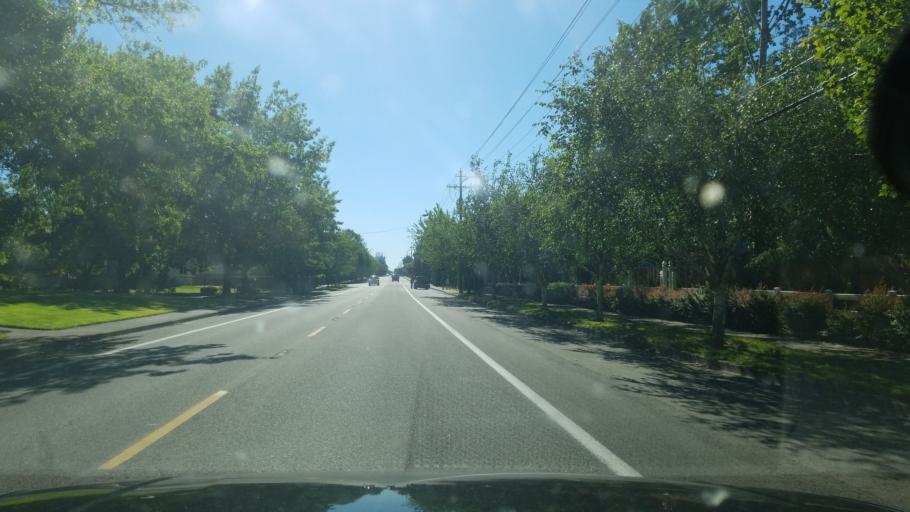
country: US
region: Oregon
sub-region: Yamhill County
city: McMinnville
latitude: 45.2264
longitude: -123.2188
